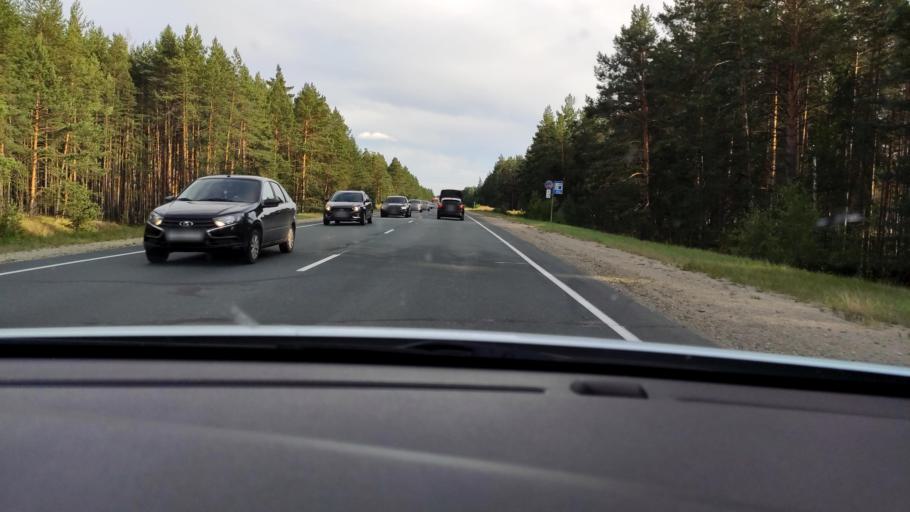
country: RU
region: Mariy-El
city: Krasnogorskiy
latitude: 56.0916
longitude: 48.3486
